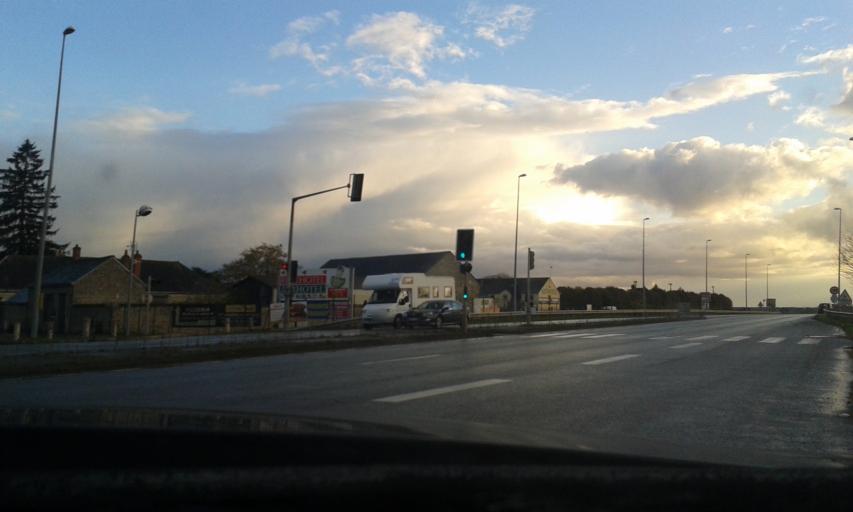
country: FR
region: Centre
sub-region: Departement du Loiret
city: Artenay
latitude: 48.0833
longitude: 1.8741
